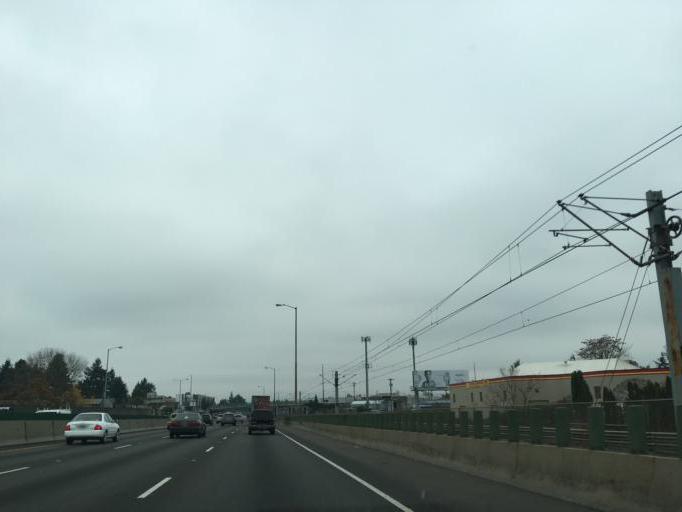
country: US
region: Oregon
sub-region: Multnomah County
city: Lents
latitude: 45.5312
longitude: -122.5979
